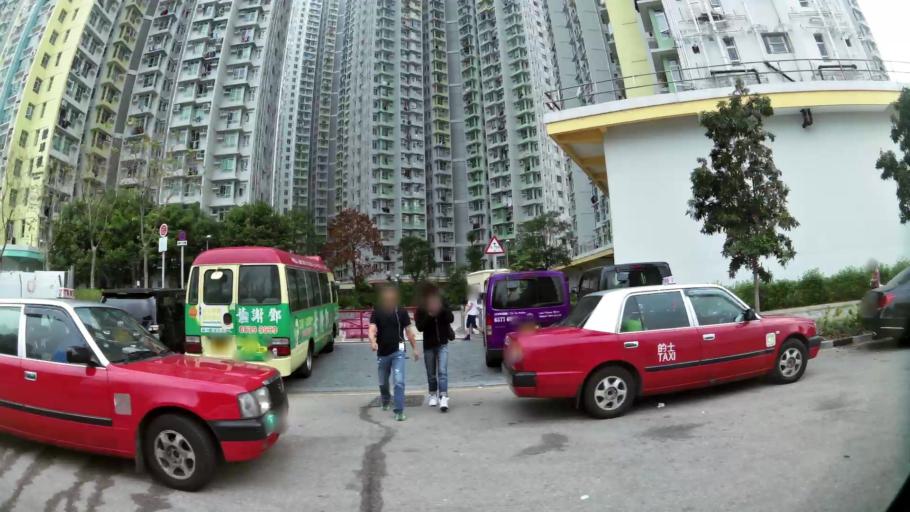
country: HK
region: Kowloon City
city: Kowloon
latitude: 22.3289
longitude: 114.2031
